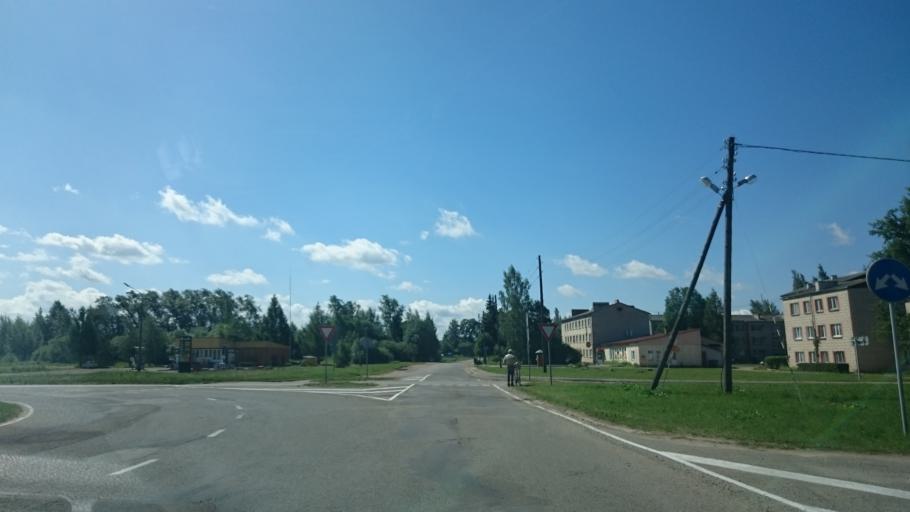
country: LV
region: Ludzas Rajons
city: Ludza
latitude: 56.5305
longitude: 27.7366
